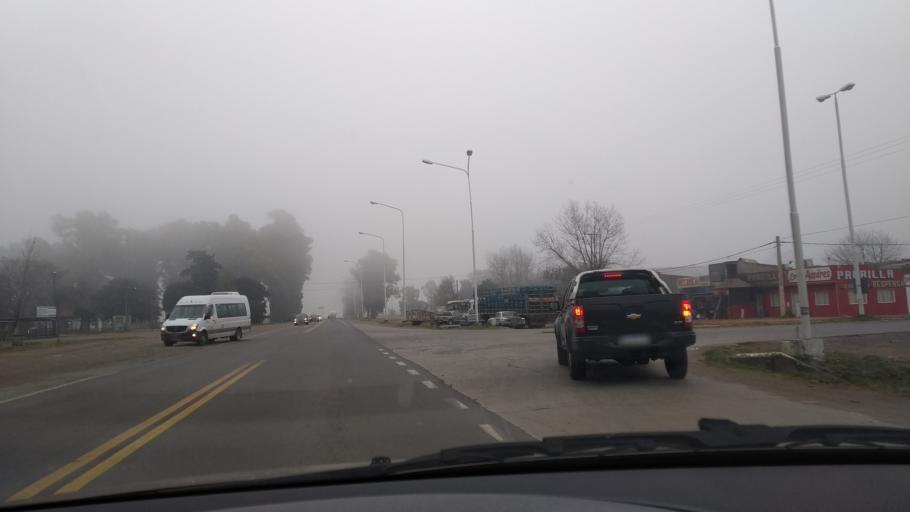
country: AR
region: Buenos Aires
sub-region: Partido de Azul
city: Azul
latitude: -36.7964
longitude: -59.8457
